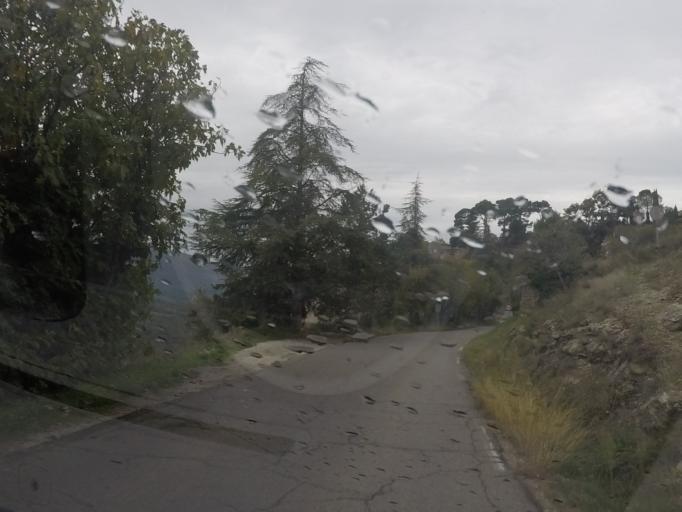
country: FR
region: Provence-Alpes-Cote d'Azur
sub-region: Departement du Vaucluse
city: Bonnieux
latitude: 43.8232
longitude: 5.3136
